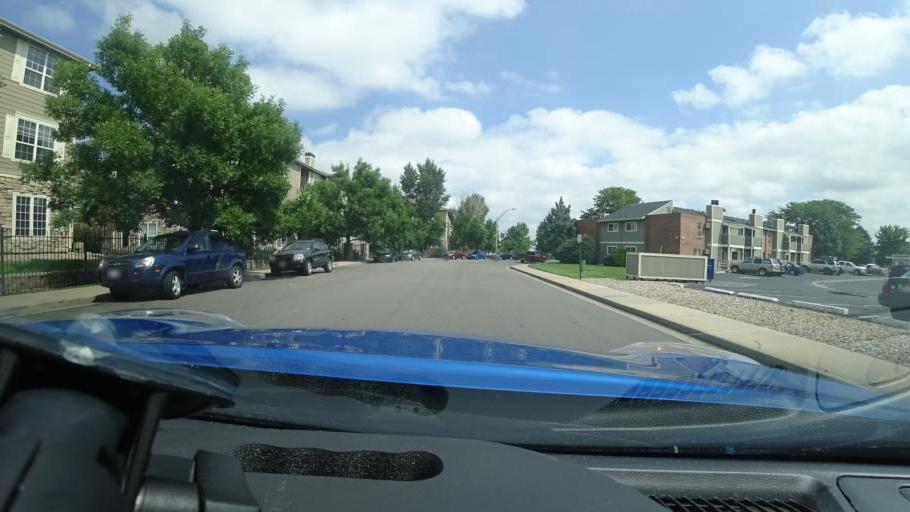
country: US
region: Colorado
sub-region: Adams County
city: Aurora
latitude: 39.7080
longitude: -104.8707
